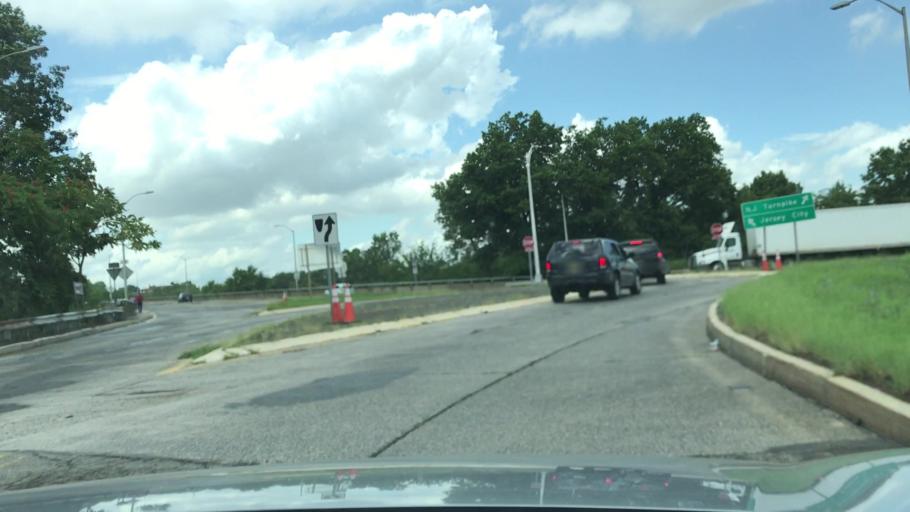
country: US
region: New Jersey
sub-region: Hudson County
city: Jersey City
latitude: 40.7015
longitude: -74.0695
